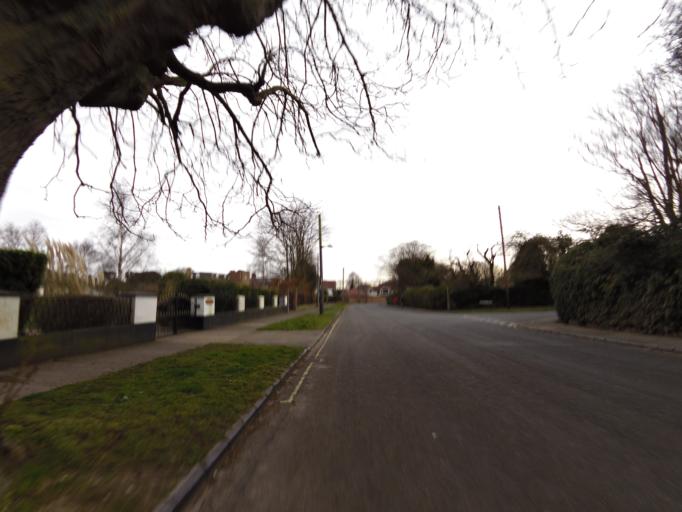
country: GB
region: England
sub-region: Suffolk
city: Felixstowe
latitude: 51.9678
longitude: 1.3712
